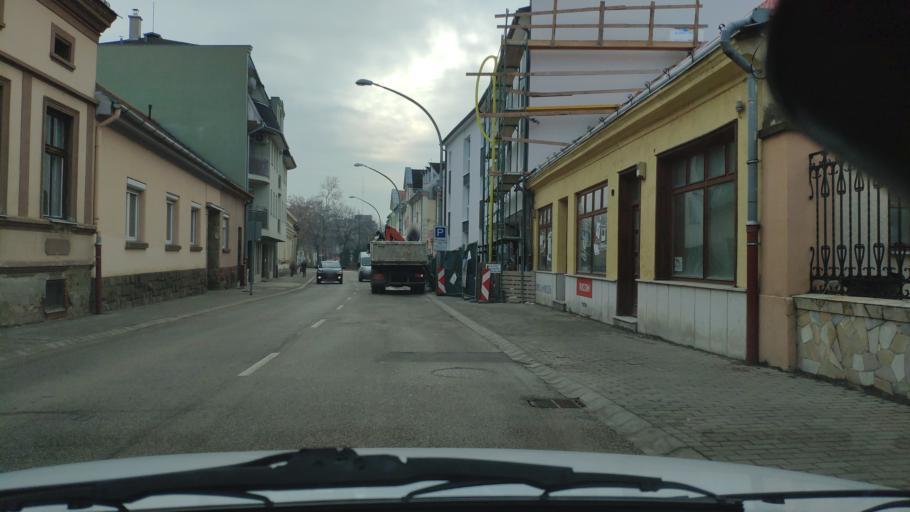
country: HU
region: Zala
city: Nagykanizsa
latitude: 46.4586
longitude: 16.9871
